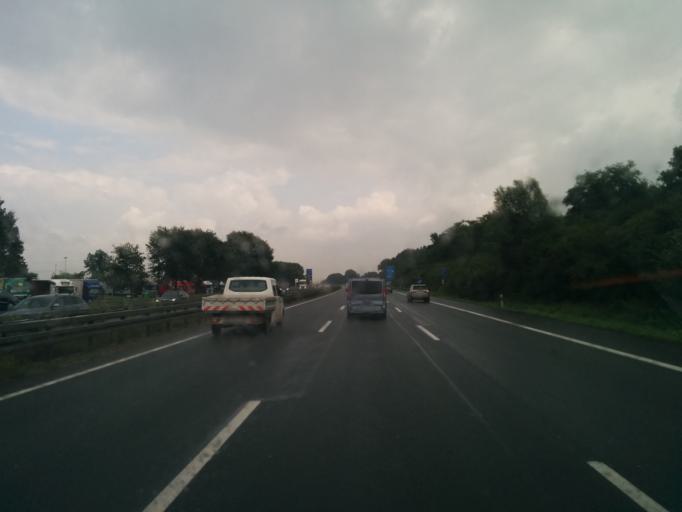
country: DE
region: Lower Saxony
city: Garbsen
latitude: 52.4214
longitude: 9.5543
